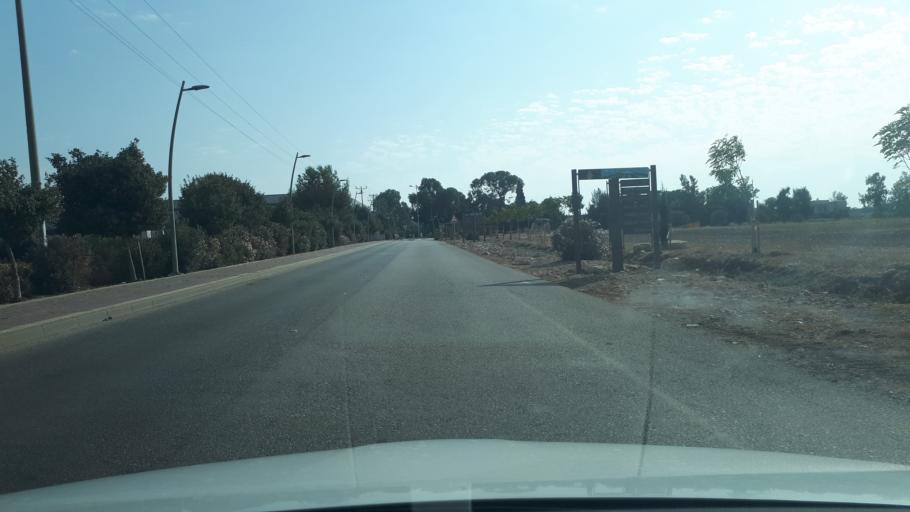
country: IL
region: Central District
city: Rosh Ha'Ayin
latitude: 32.0866
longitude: 34.9420
